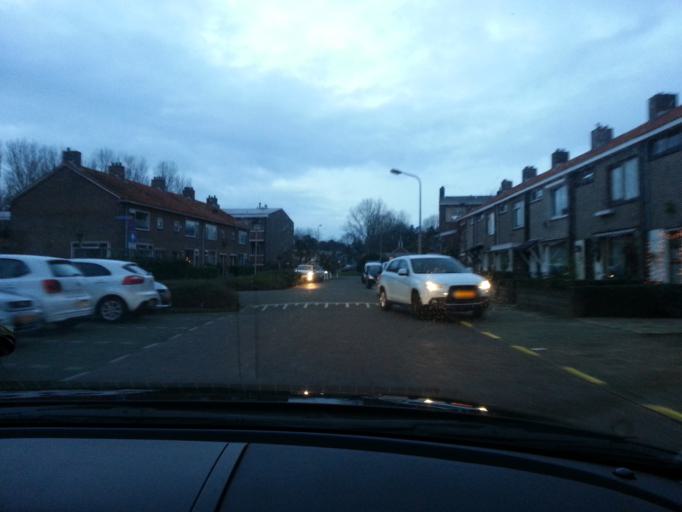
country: NL
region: South Holland
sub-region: Gemeente Katwijk
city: Katwijk aan den Rijn
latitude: 52.1982
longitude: 4.4148
